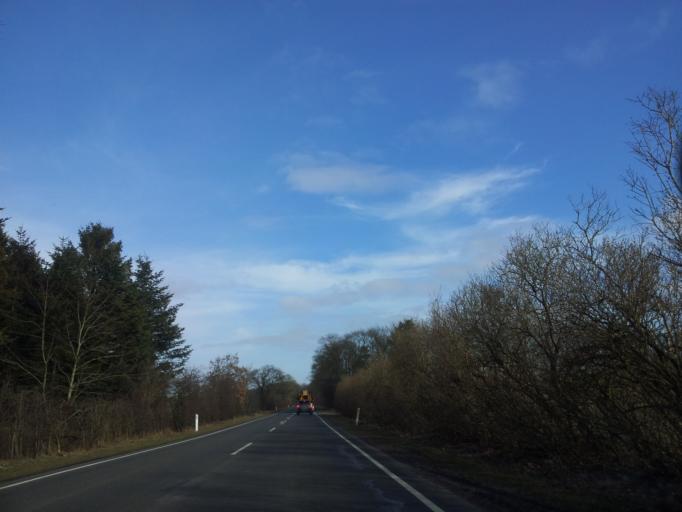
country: DK
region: South Denmark
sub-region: Vejen Kommune
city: Brorup
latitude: 55.4445
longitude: 9.0248
